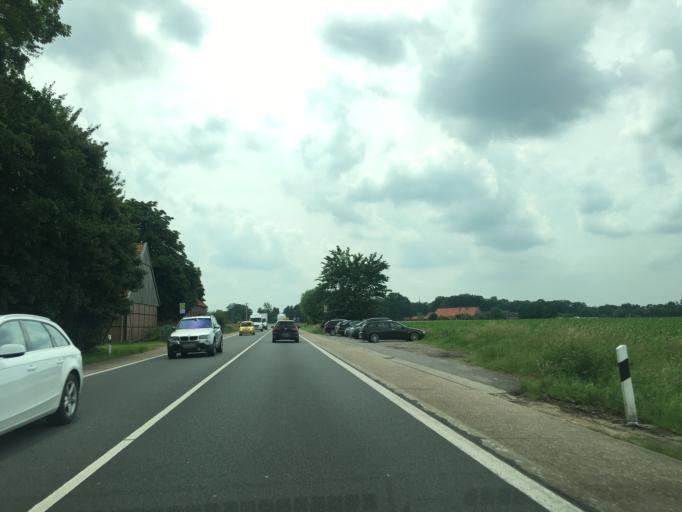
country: DE
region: North Rhine-Westphalia
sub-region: Regierungsbezirk Munster
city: Steinfurt
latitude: 52.1680
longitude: 7.3448
